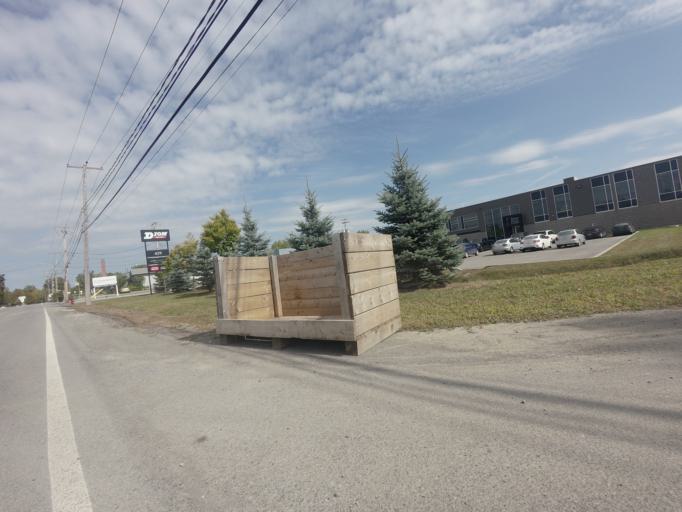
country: CA
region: Quebec
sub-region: Laurentides
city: Blainville
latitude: 45.6275
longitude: -73.9024
